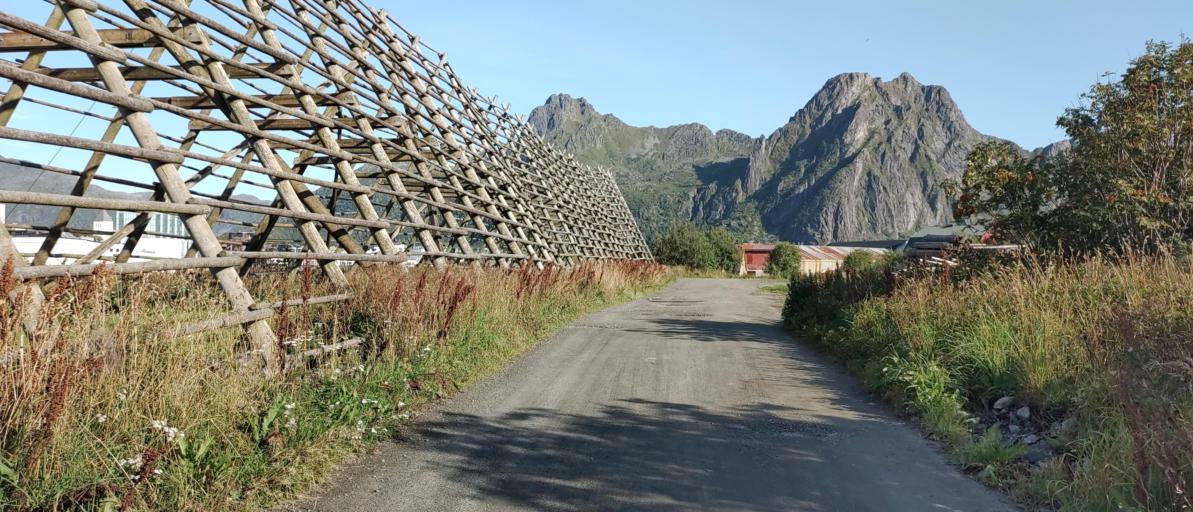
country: NO
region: Nordland
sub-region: Vagan
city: Svolvaer
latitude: 68.2272
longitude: 14.5687
